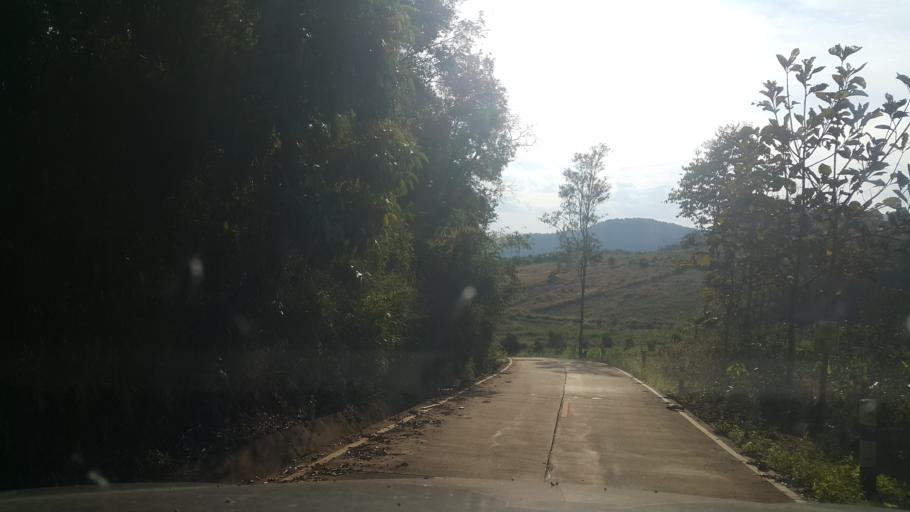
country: TH
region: Chiang Mai
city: Samoeng
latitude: 19.0041
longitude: 98.6872
